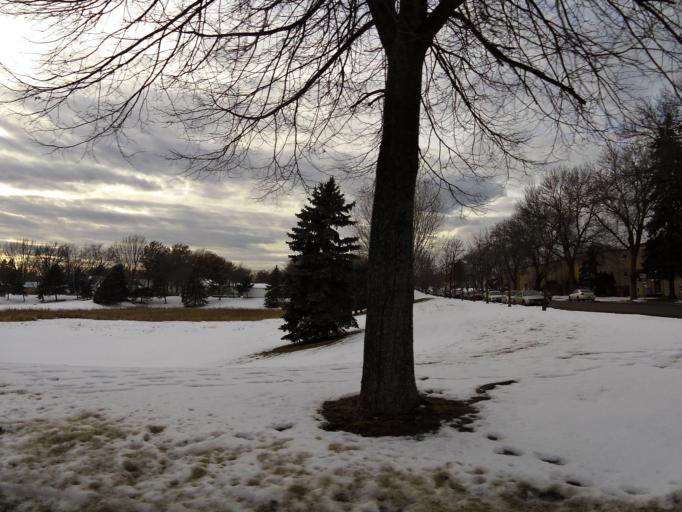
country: US
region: Minnesota
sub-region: Ramsey County
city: Maplewood
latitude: 44.9666
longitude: -93.0203
